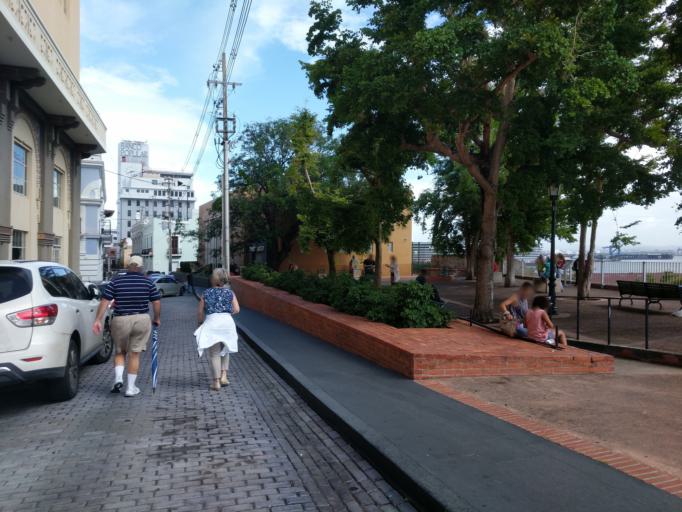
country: PR
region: San Juan
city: San Juan
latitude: 18.4640
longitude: -66.1171
